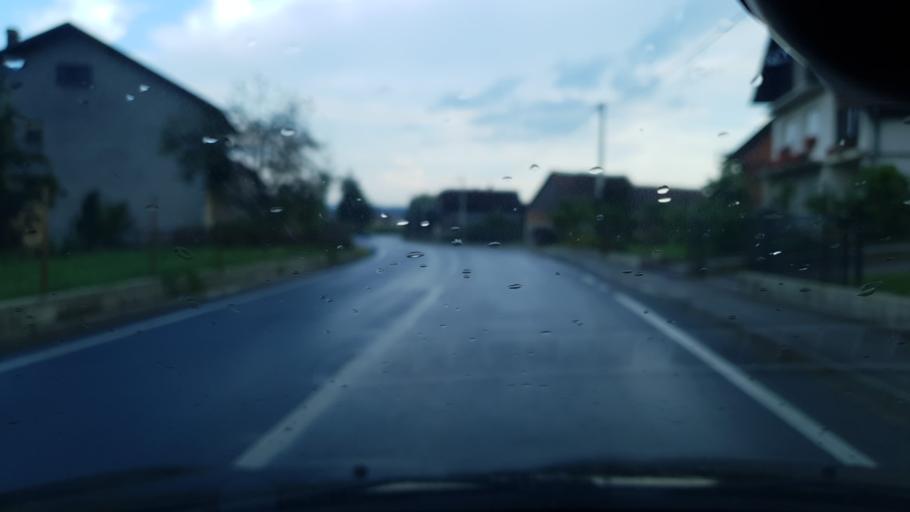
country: HR
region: Krapinsko-Zagorska
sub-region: Grad Krapina
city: Krapina
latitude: 46.0991
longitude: 15.9056
